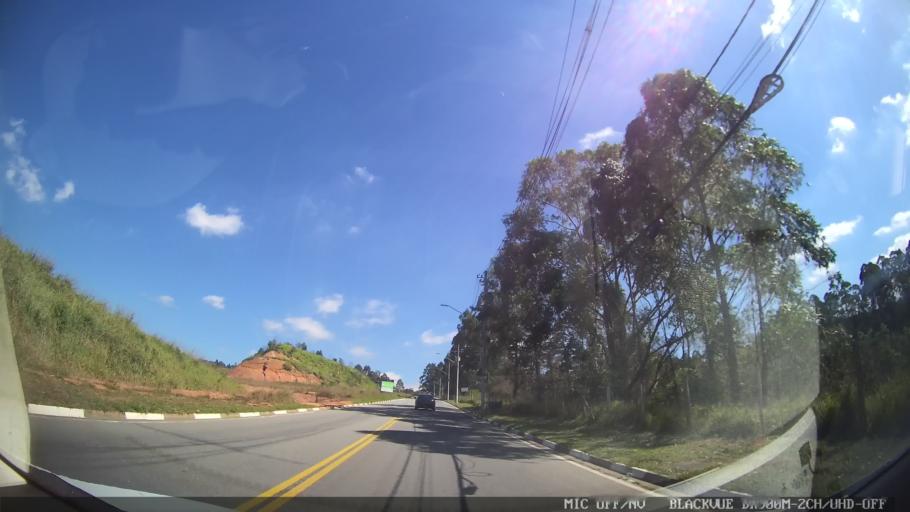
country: BR
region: Sao Paulo
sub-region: Barueri
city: Barueri
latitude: -23.4436
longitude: -46.8343
